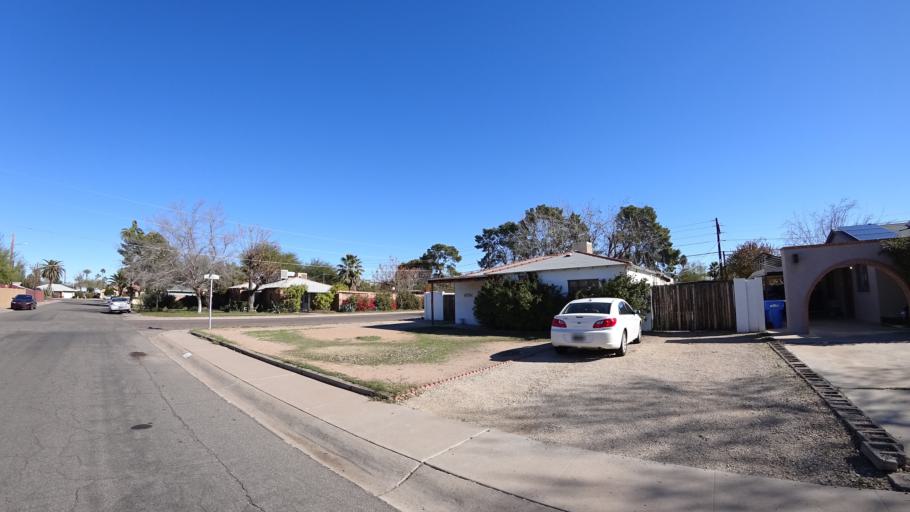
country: US
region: Arizona
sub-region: Maricopa County
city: Phoenix
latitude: 33.4999
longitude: -112.0400
